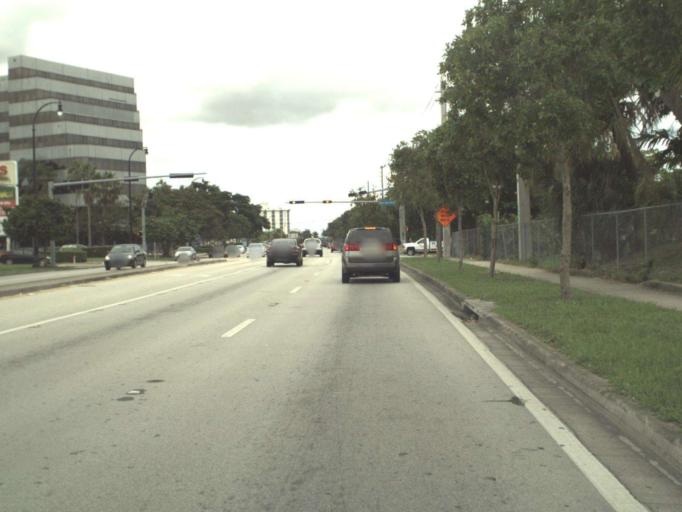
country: US
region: Florida
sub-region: Miami-Dade County
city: Biscayne Park
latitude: 25.8845
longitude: -80.1652
